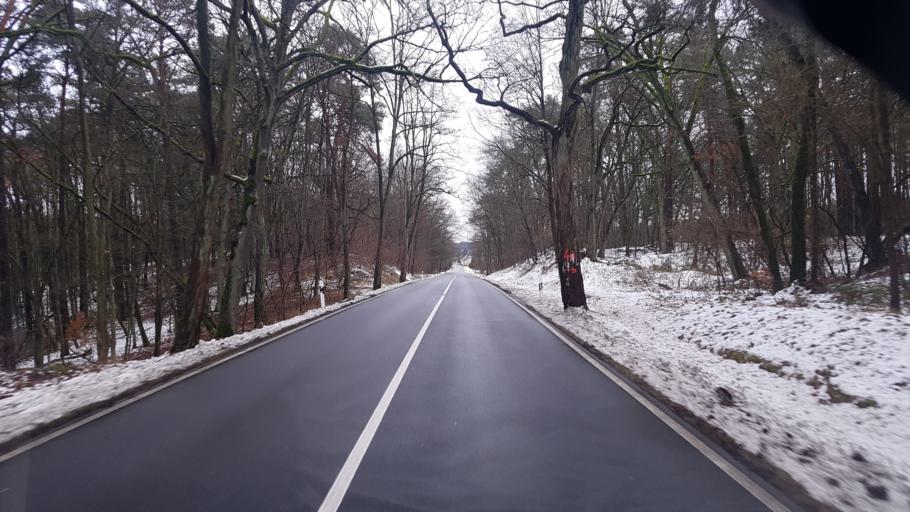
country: DE
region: Brandenburg
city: Schenkendobern
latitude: 51.9736
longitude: 14.5615
